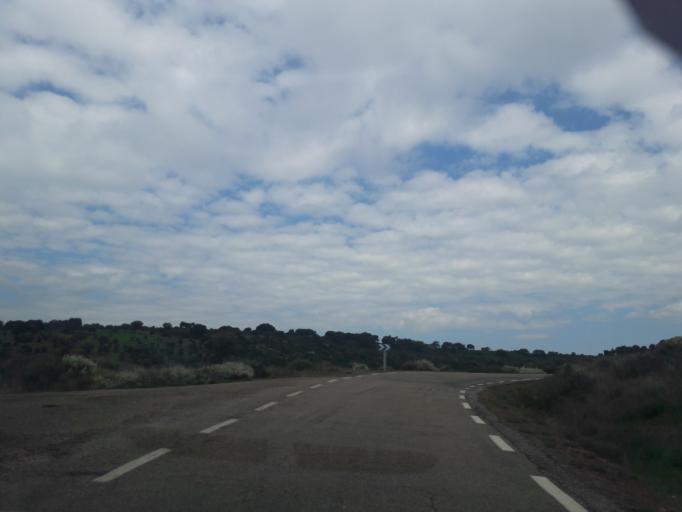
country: ES
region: Castille and Leon
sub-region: Provincia de Salamanca
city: Serradilla del Arroyo
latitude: 40.5249
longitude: -6.3818
